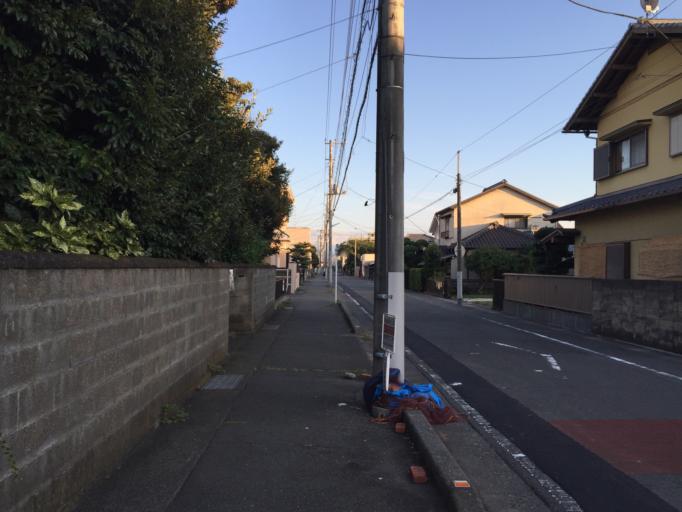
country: JP
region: Shizuoka
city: Numazu
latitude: 35.0931
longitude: 138.8636
